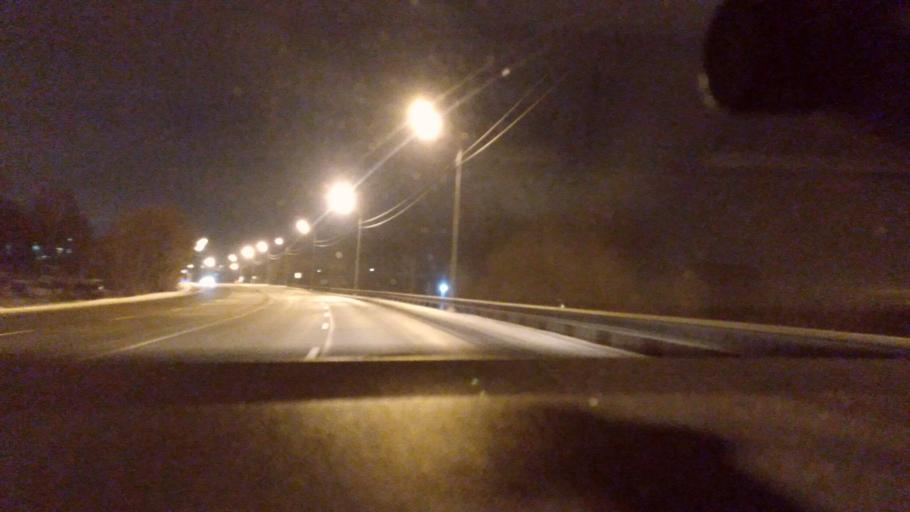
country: RU
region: Moskovskaya
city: Bronnitsy
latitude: 55.4673
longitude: 38.1996
